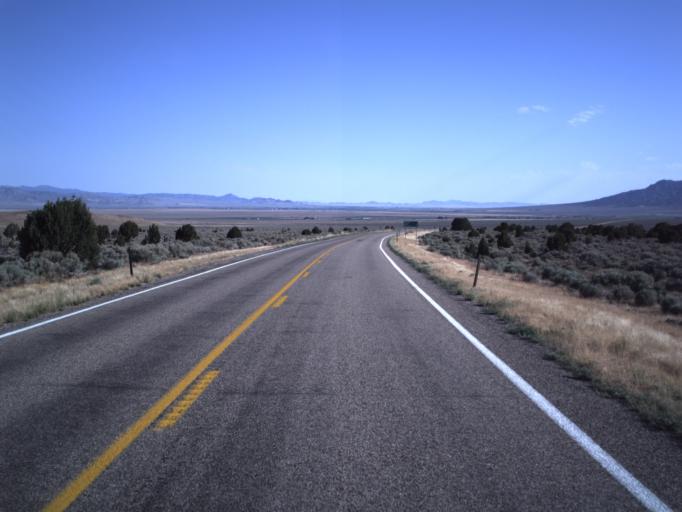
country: US
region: Utah
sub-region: Beaver County
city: Milford
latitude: 38.1325
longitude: -112.9598
